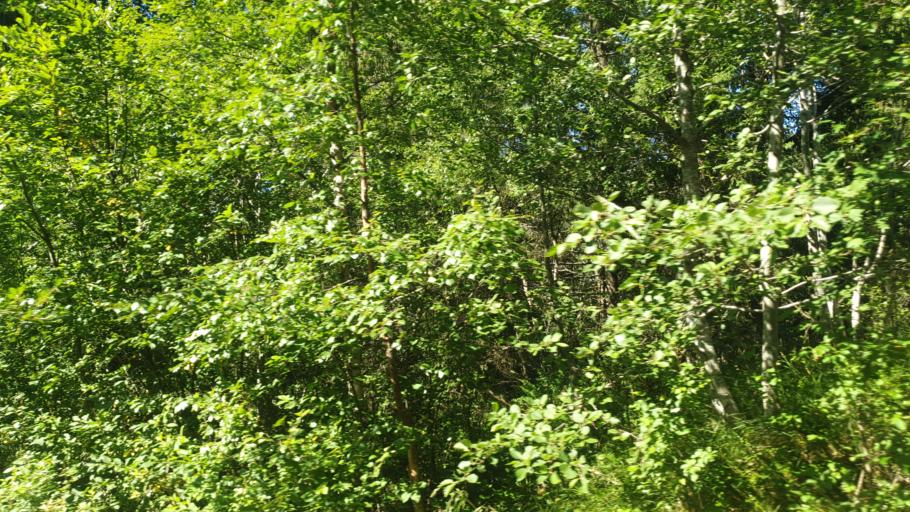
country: NO
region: Sor-Trondelag
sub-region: Meldal
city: Meldal
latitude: 63.1651
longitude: 9.7347
